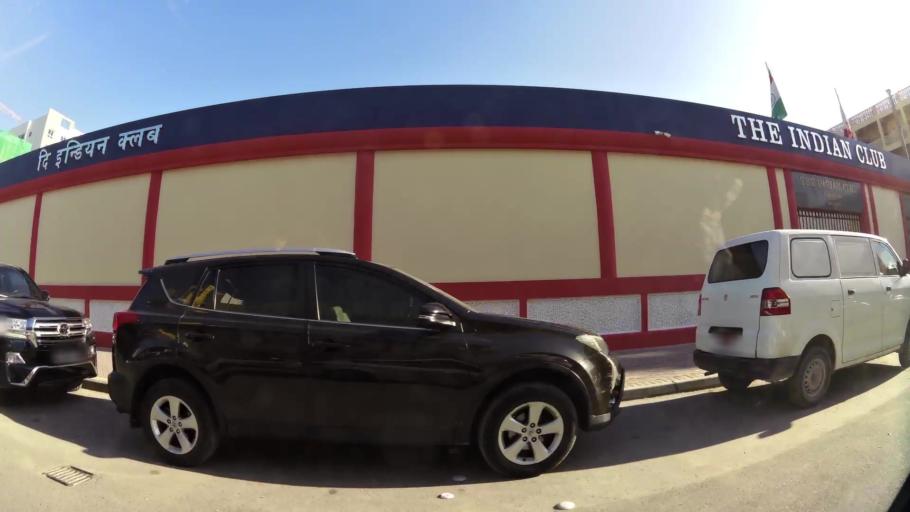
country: BH
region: Manama
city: Manama
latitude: 26.2281
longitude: 50.5830
